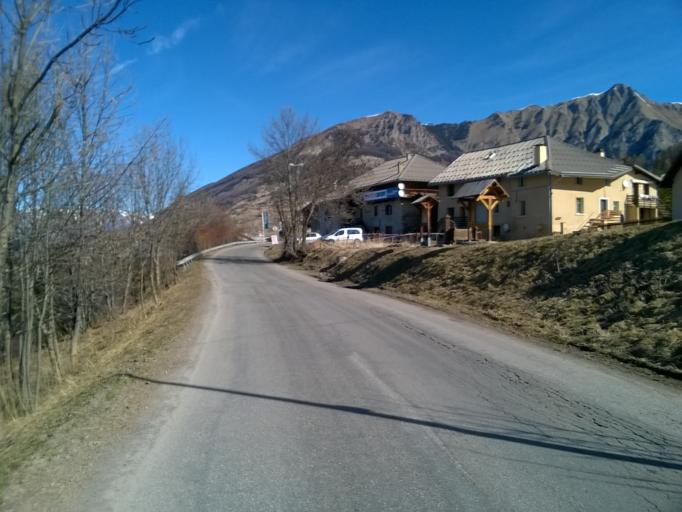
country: FR
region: Provence-Alpes-Cote d'Azur
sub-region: Departement des Hautes-Alpes
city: Embrun
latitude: 44.4986
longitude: 6.5553
